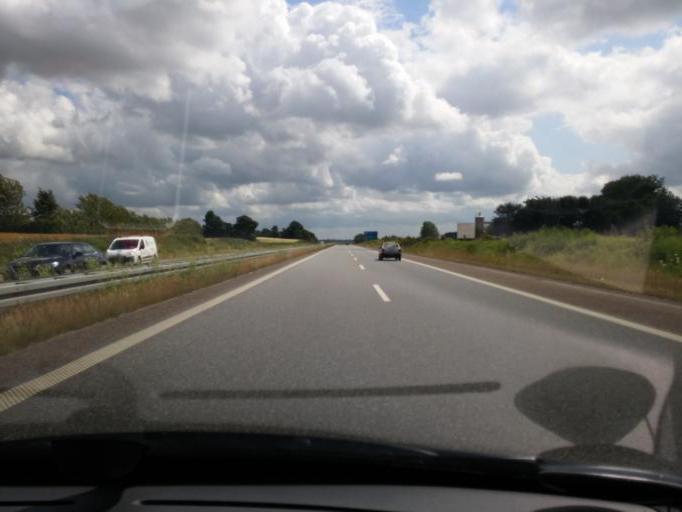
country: DK
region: South Denmark
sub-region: Faaborg-Midtfyn Kommune
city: Ringe
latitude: 55.2076
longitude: 10.5095
